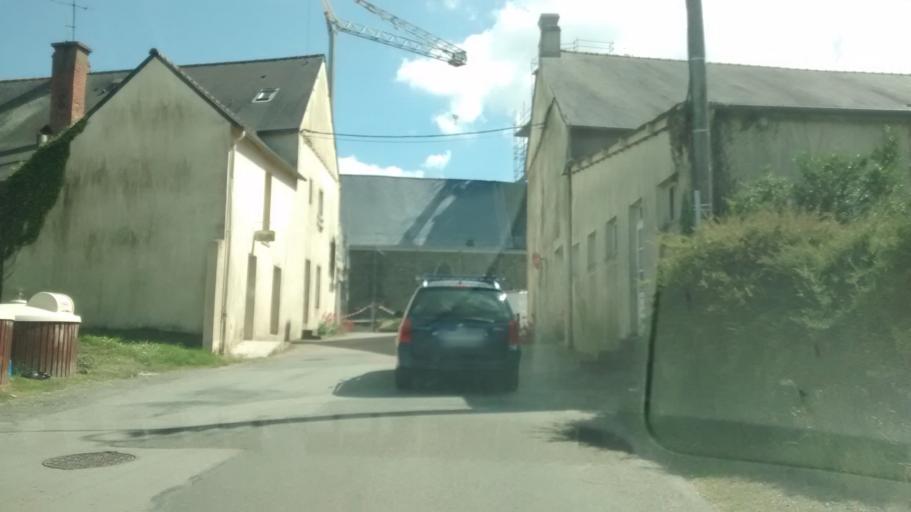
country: FR
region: Brittany
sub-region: Departement du Morbihan
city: Caro
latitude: 47.8648
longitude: -2.3189
